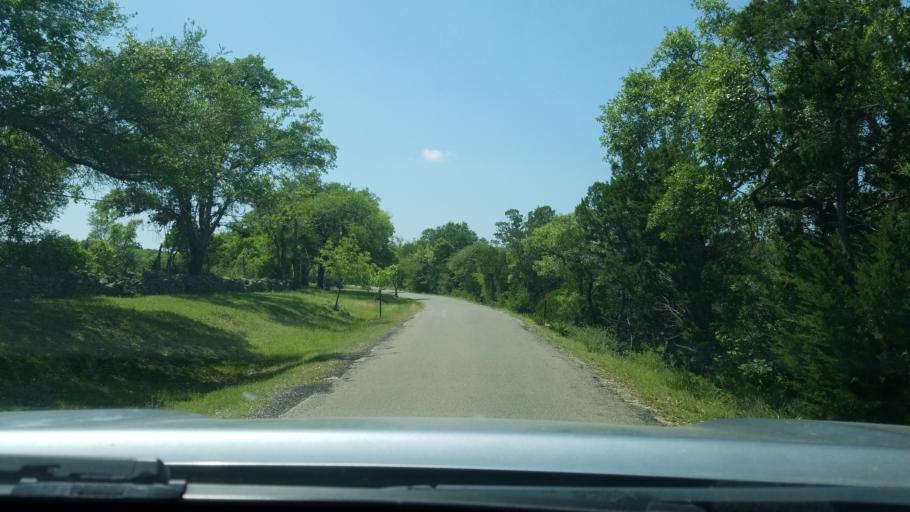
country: US
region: Texas
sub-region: Blanco County
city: Blanco
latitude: 30.0041
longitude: -98.4276
